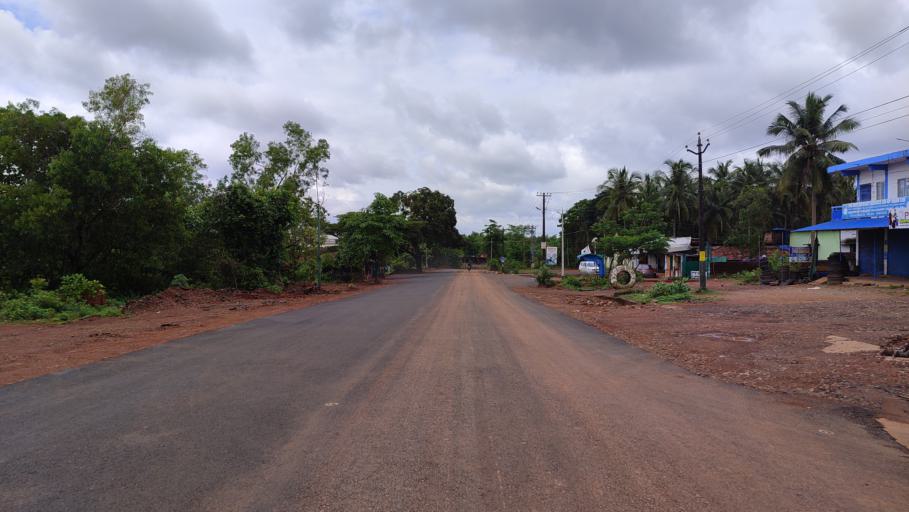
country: IN
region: Kerala
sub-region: Kasaragod District
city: Kasaragod
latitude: 12.5345
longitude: 75.0718
